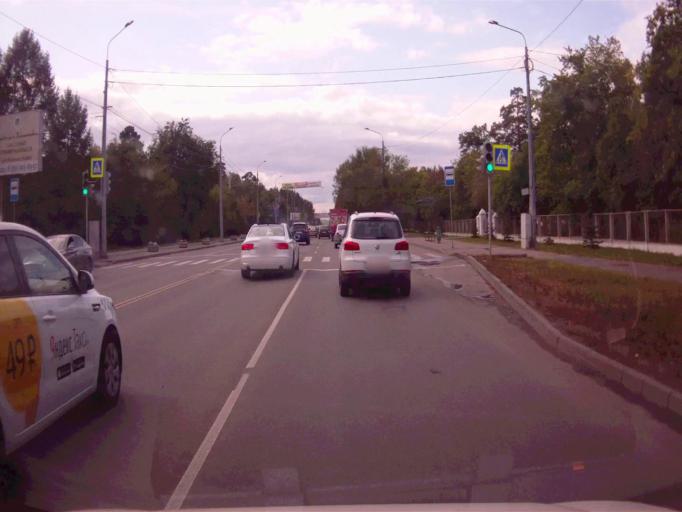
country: RU
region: Chelyabinsk
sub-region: Gorod Chelyabinsk
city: Chelyabinsk
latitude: 55.1473
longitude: 61.3589
